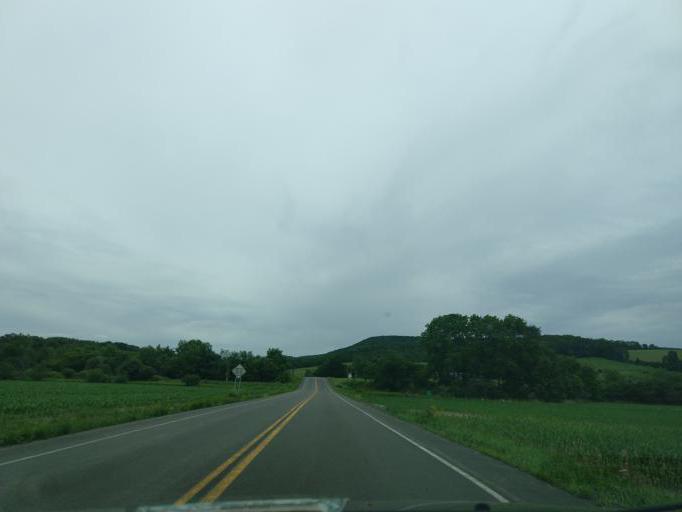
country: US
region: New York
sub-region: Cortland County
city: Munsons Corners
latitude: 42.5014
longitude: -76.2119
